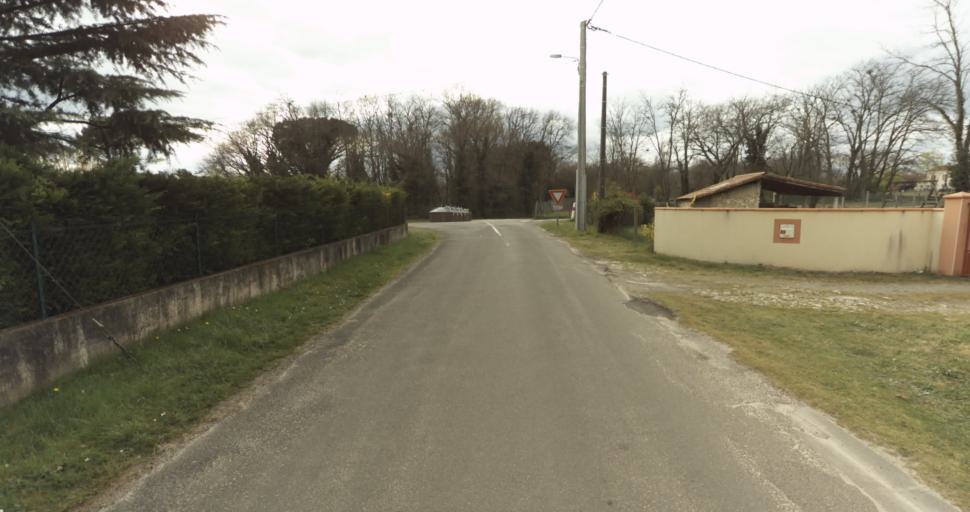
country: FR
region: Aquitaine
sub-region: Departement des Landes
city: Roquefort
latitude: 44.0381
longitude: -0.3278
